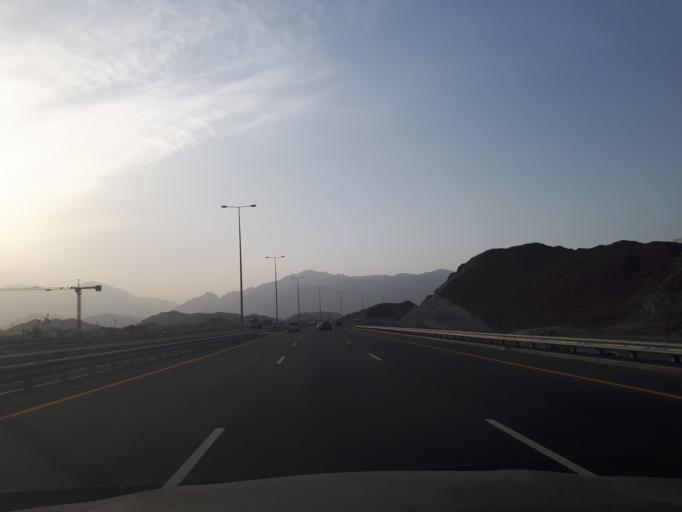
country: OM
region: Muhafazat ad Dakhiliyah
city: Bidbid
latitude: 23.3483
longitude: 58.0934
